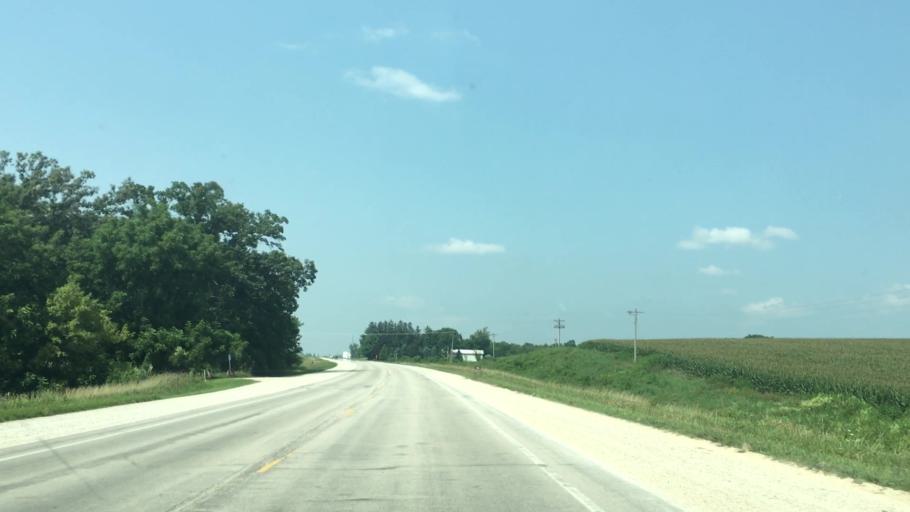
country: US
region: Iowa
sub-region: Winneshiek County
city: Decorah
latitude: 43.4259
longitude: -91.8592
